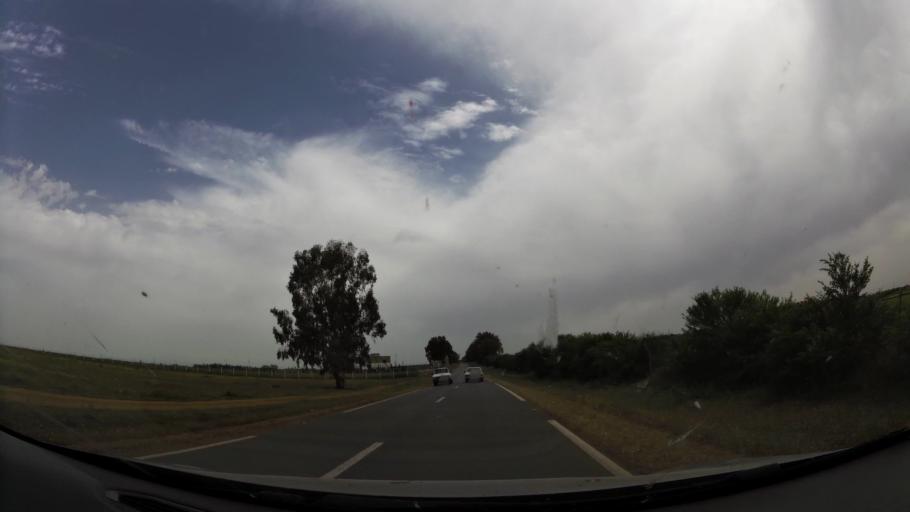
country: MA
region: Rabat-Sale-Zemmour-Zaer
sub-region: Khemisset
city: Tiflet
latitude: 33.8254
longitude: -6.2722
